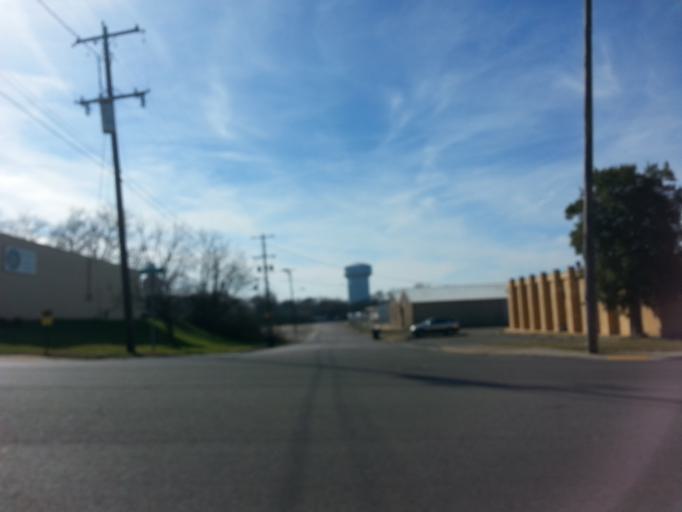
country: US
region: Tennessee
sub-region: Rutherford County
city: Murfreesboro
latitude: 35.8408
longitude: -86.3922
